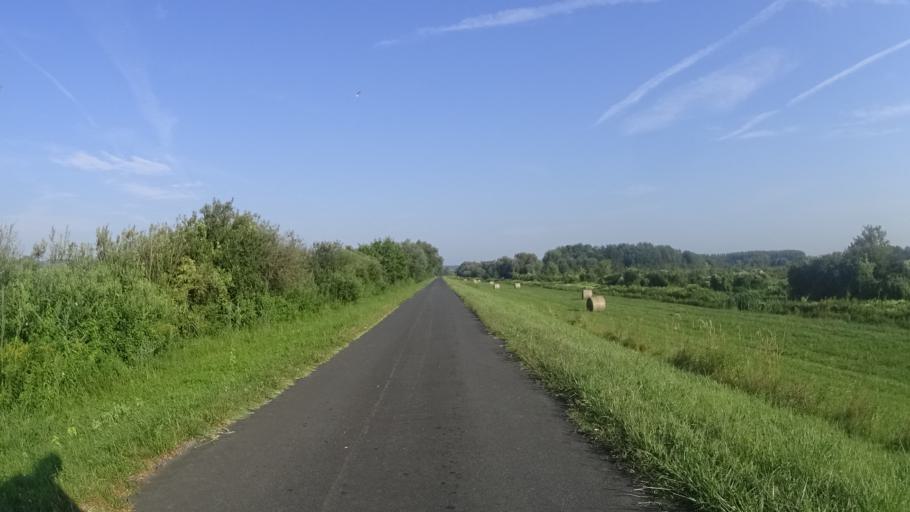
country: HU
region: Zala
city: Sarmellek
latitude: 46.6537
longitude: 17.1431
